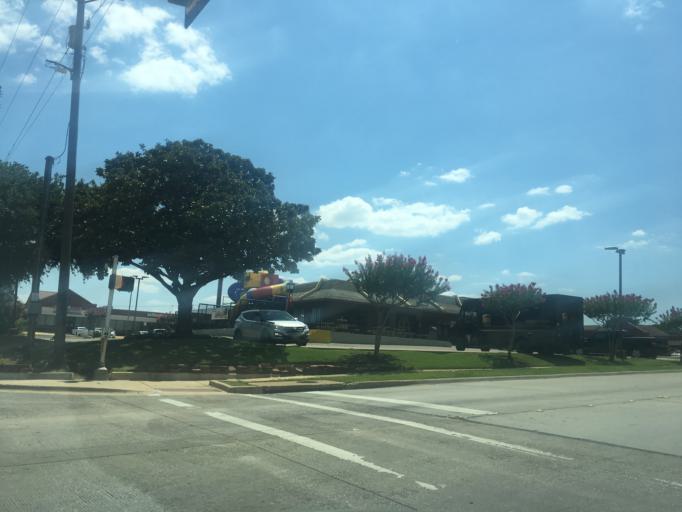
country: US
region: Texas
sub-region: Denton County
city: Lewisville
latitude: 33.0141
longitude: -96.9932
